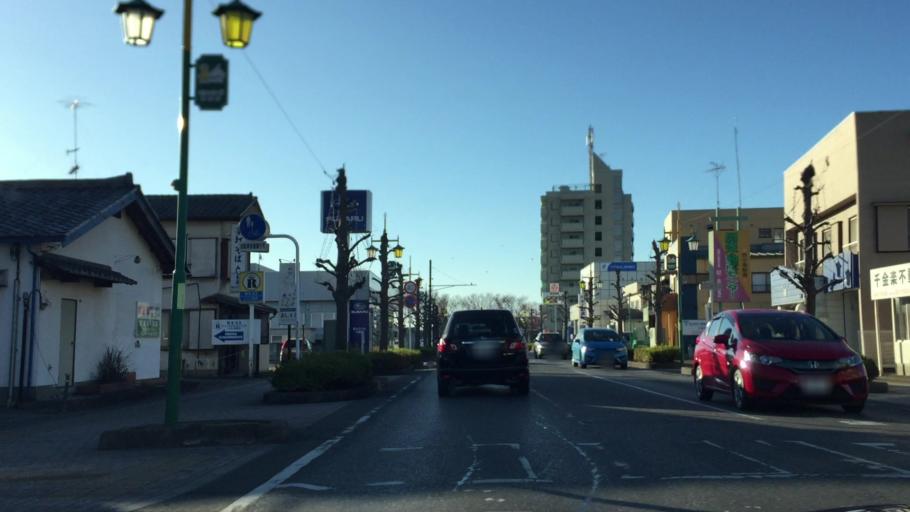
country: JP
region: Saitama
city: Menuma
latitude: 36.2596
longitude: 139.4072
